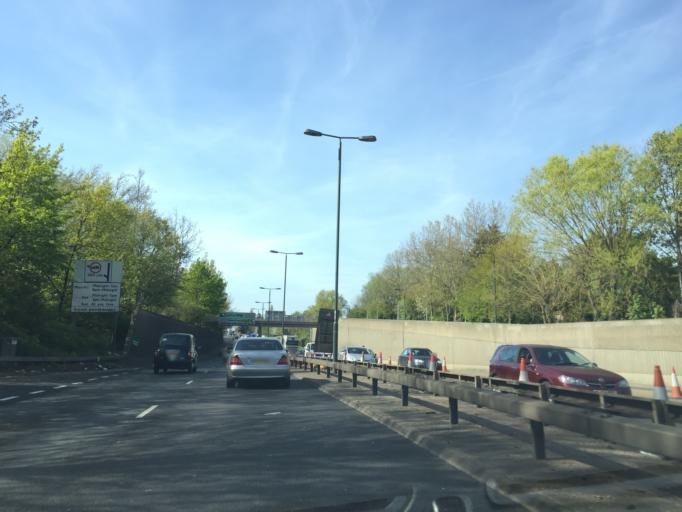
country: GB
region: England
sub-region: Greater London
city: Blackheath
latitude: 51.4685
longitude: 0.0285
